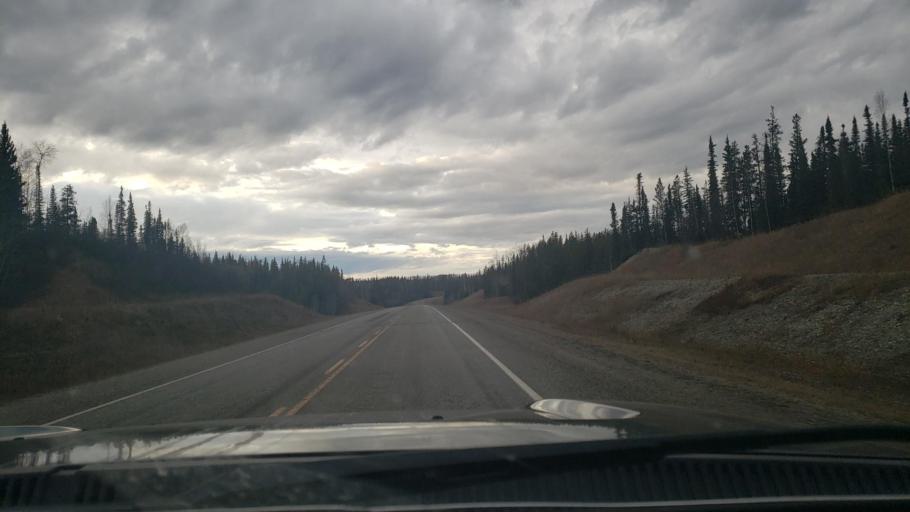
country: CA
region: Yukon
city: Watson Lake
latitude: 59.9807
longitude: -127.5779
